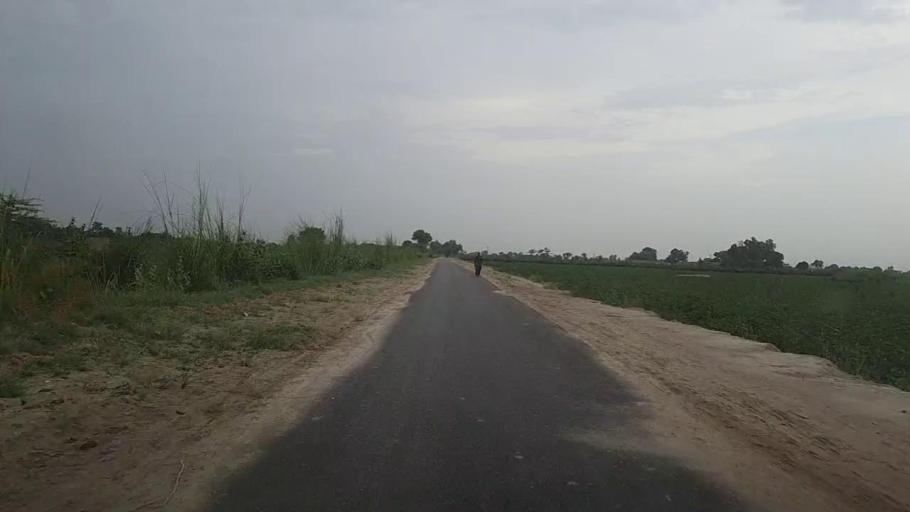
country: PK
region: Sindh
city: Karaundi
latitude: 26.9868
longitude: 68.3541
